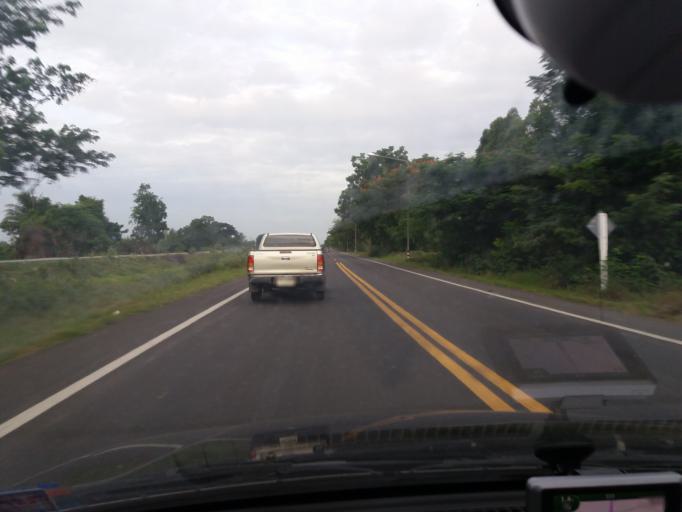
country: TH
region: Suphan Buri
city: U Thong
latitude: 14.5205
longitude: 99.9251
